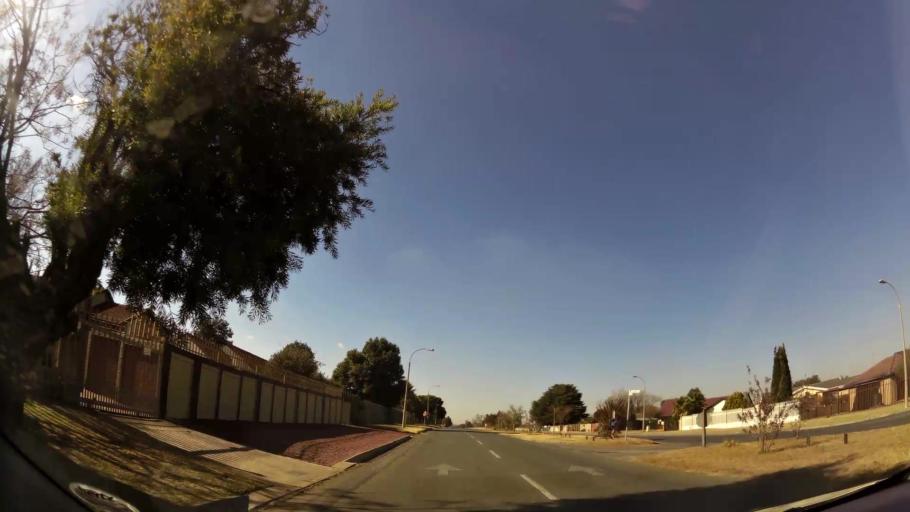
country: ZA
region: Gauteng
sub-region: City of Johannesburg Metropolitan Municipality
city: Roodepoort
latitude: -26.1485
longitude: 27.8259
